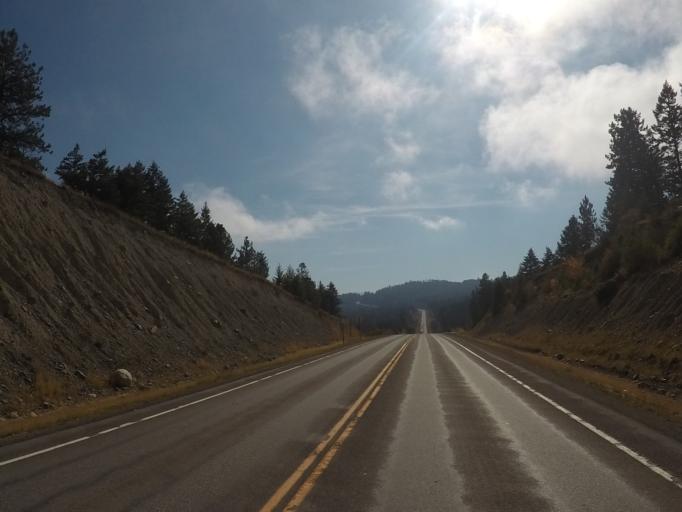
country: US
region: Montana
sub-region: Flathead County
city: Lakeside
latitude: 48.0070
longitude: -114.2191
